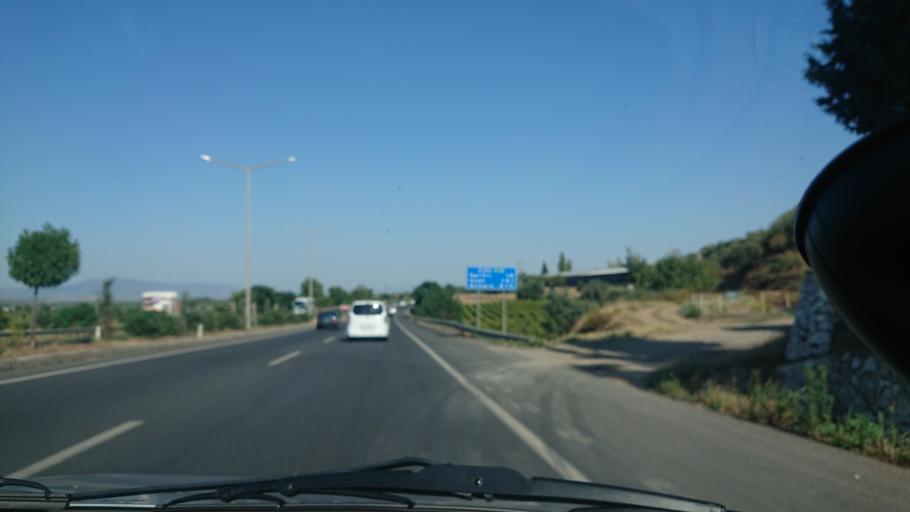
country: TR
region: Manisa
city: Ahmetli
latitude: 38.5154
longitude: 27.9464
